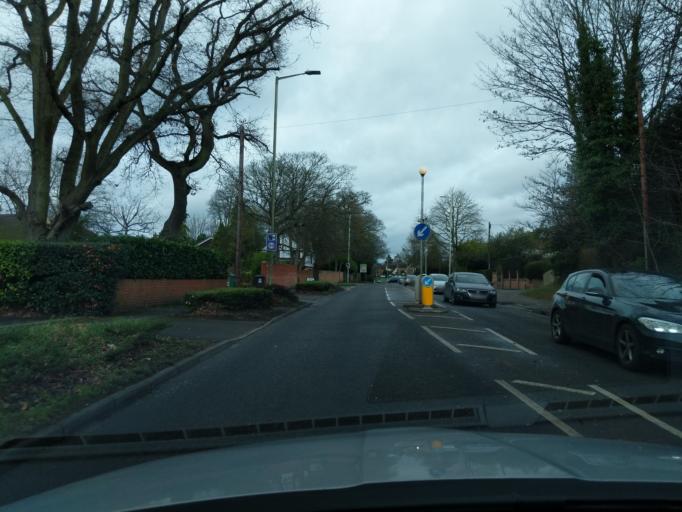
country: GB
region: England
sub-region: Hertfordshire
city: Watford
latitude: 51.6747
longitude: -0.4196
